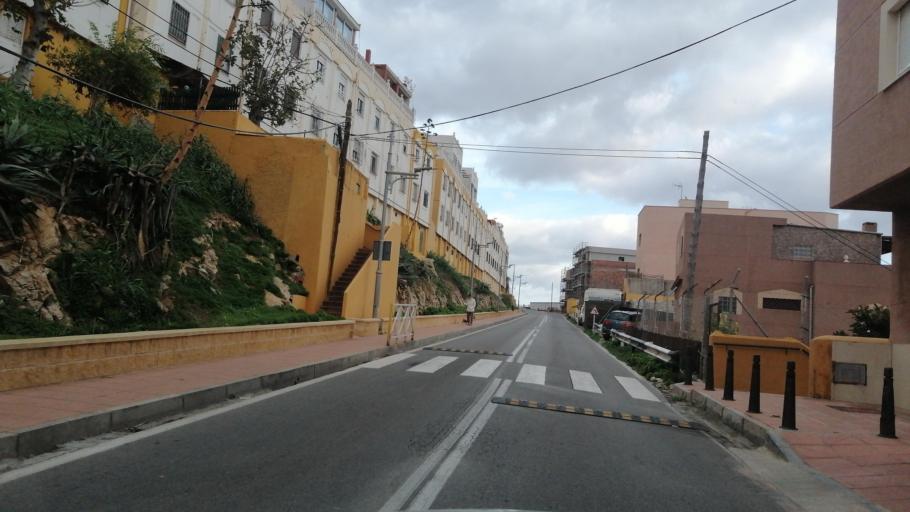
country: ES
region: Ceuta
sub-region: Ceuta
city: Ceuta
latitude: 35.8903
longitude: -5.2949
